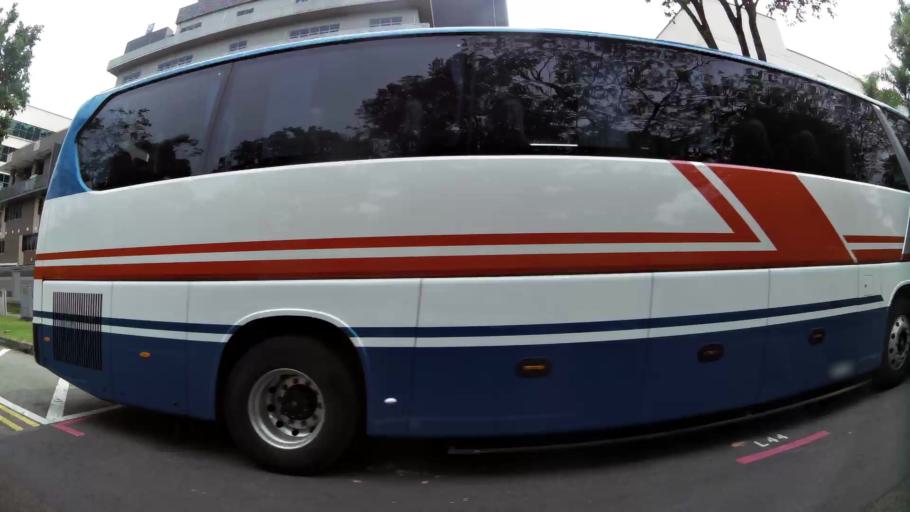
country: MY
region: Johor
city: Johor Bahru
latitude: 1.4429
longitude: 103.7826
